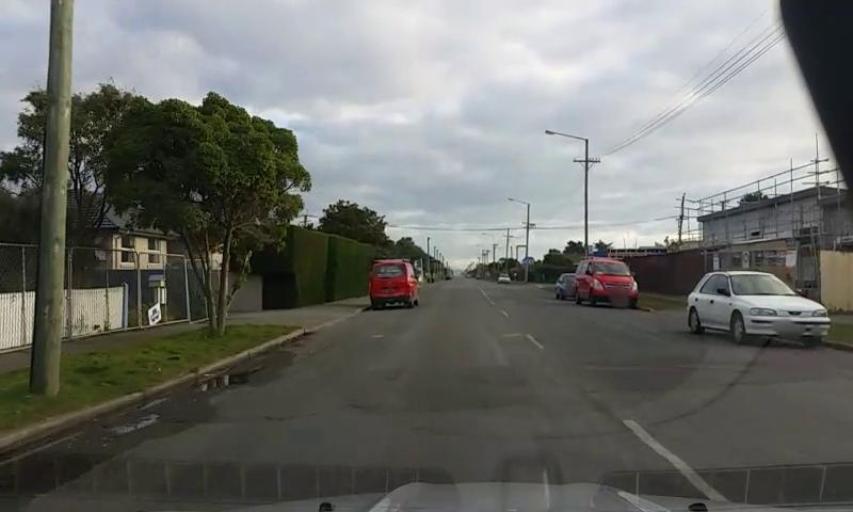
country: NZ
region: Canterbury
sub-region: Christchurch City
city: Christchurch
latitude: -43.5348
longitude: 172.7376
